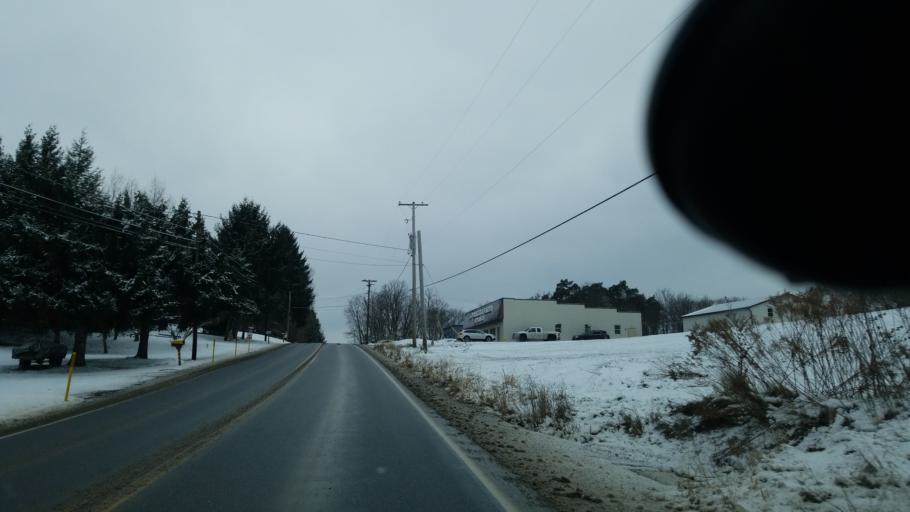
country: US
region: Pennsylvania
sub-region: Jefferson County
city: Albion
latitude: 40.9389
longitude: -78.9459
